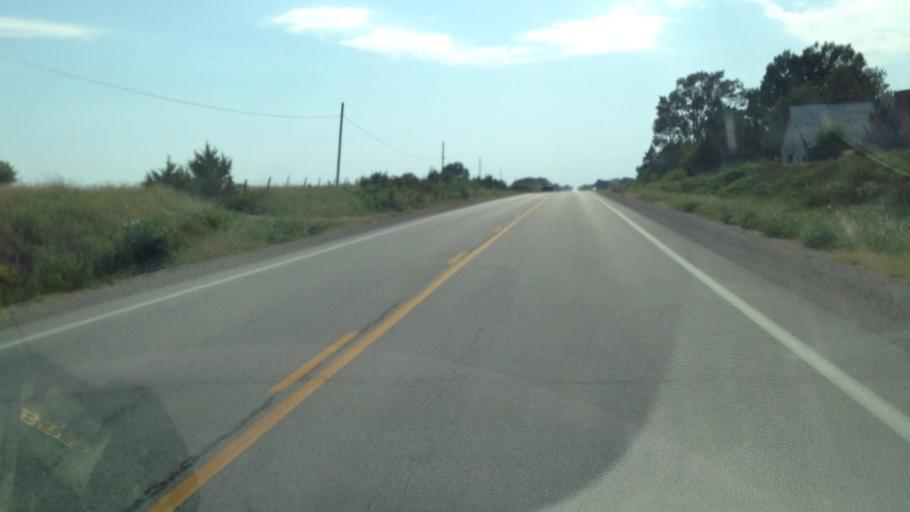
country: US
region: Kansas
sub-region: Anderson County
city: Garnett
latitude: 38.0816
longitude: -95.1823
